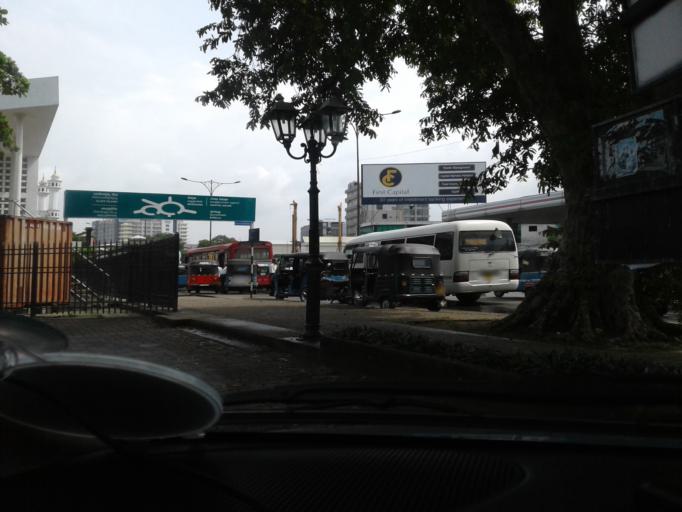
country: LK
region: Western
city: Colombo
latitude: 6.9152
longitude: 79.8647
